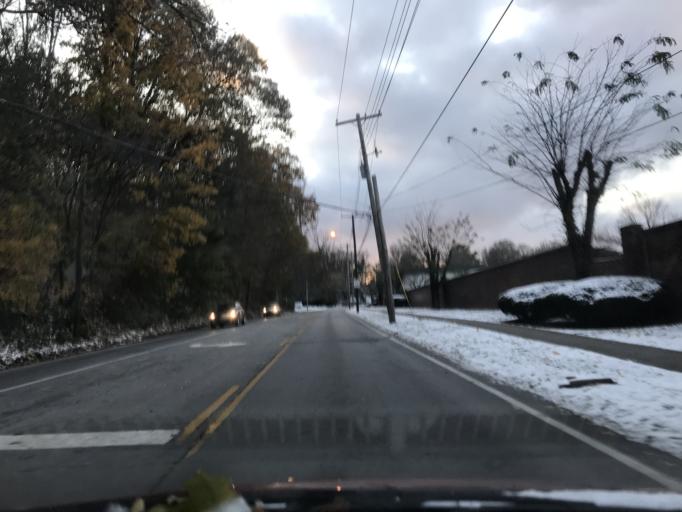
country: US
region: Indiana
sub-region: Clark County
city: Jeffersonville
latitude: 38.2595
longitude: -85.7107
